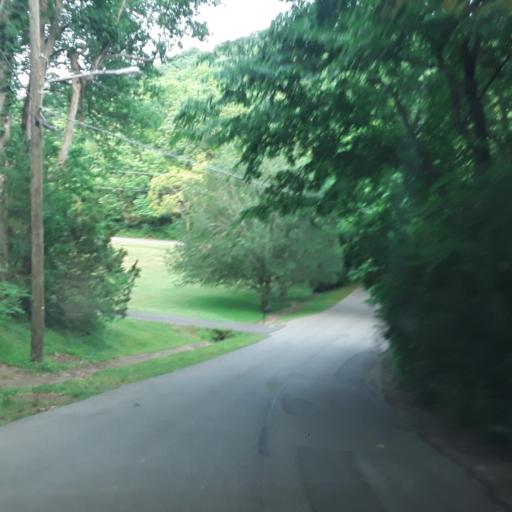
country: US
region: Tennessee
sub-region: Williamson County
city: Brentwood
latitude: 36.0494
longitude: -86.7801
